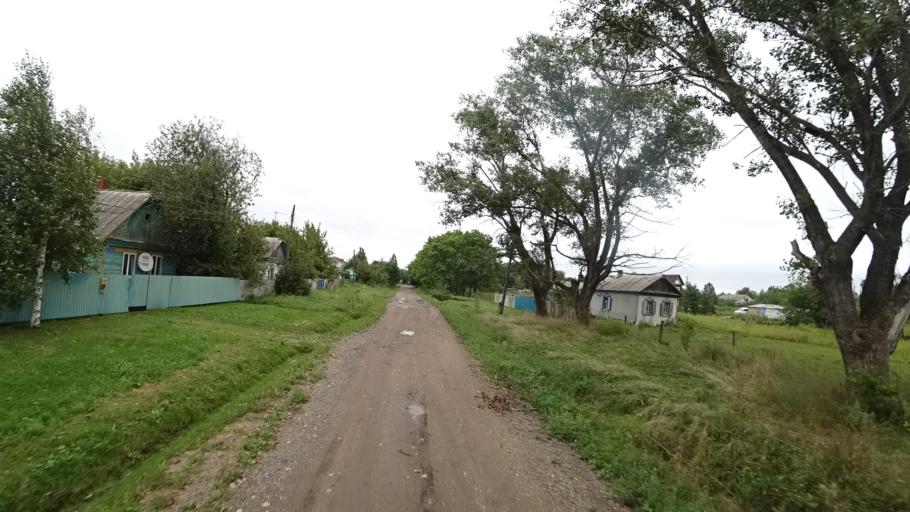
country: RU
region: Primorskiy
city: Chernigovka
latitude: 44.3382
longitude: 132.5425
